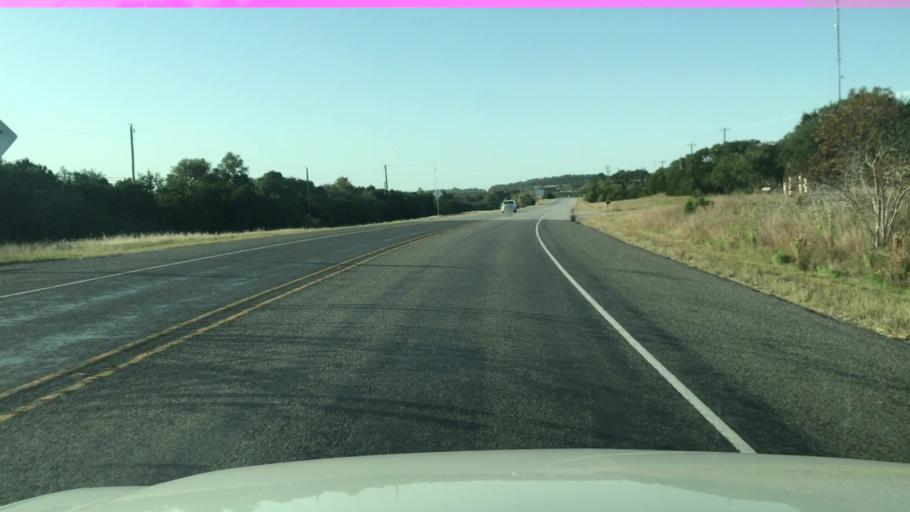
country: US
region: Texas
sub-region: Blanco County
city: Johnson City
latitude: 30.1953
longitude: -98.3758
